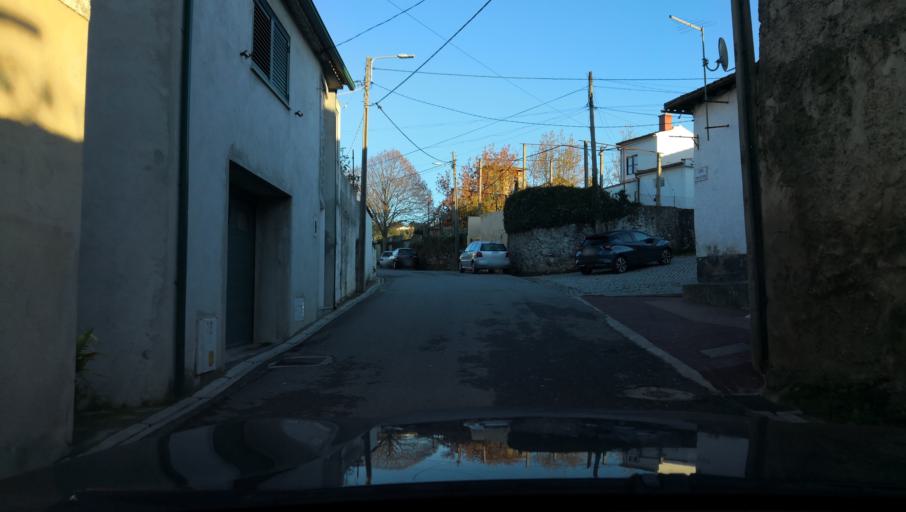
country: PT
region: Vila Real
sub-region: Vila Real
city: Vila Real
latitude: 41.2805
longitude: -7.7398
